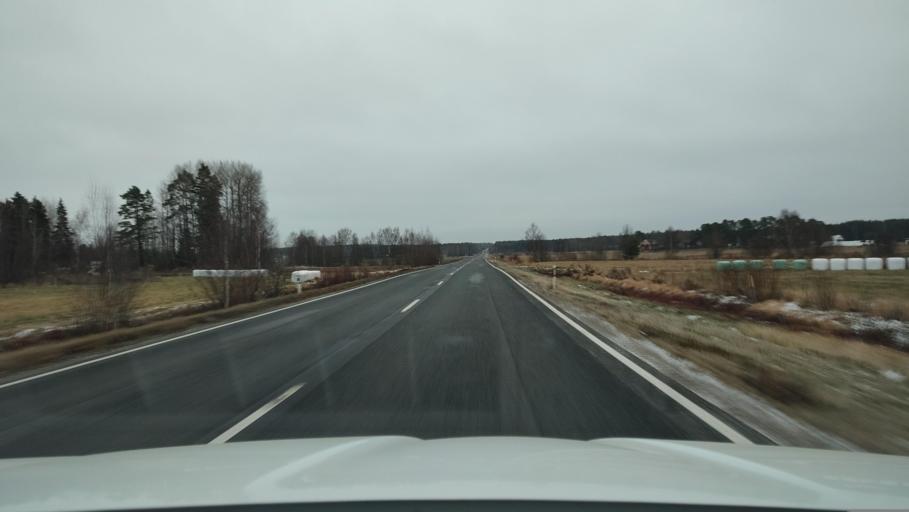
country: FI
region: Ostrobothnia
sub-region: Sydosterbotten
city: Naerpes
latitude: 62.4017
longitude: 21.3768
